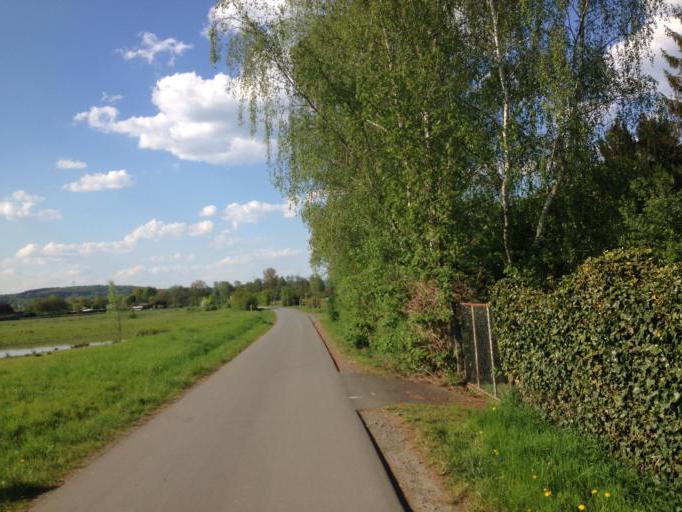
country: DE
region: Hesse
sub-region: Regierungsbezirk Giessen
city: Giessen
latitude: 50.6032
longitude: 8.6711
